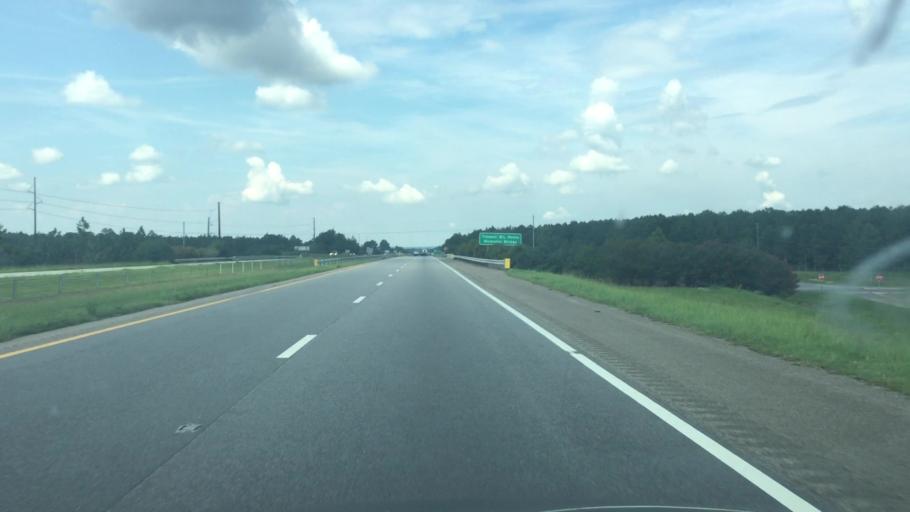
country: US
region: North Carolina
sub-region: Richmond County
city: Hamlet
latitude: 34.8563
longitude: -79.6935
